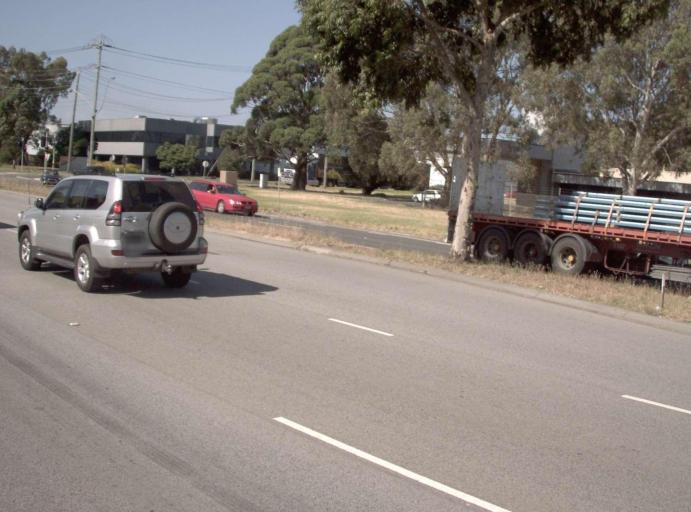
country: AU
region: Victoria
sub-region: Casey
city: Hampton Park
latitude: -38.0325
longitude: 145.2117
